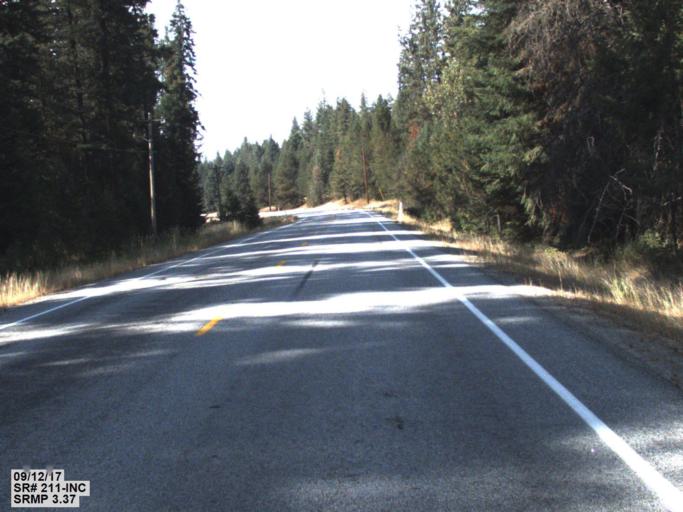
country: US
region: Washington
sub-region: Pend Oreille County
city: Newport
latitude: 48.1419
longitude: -117.2901
